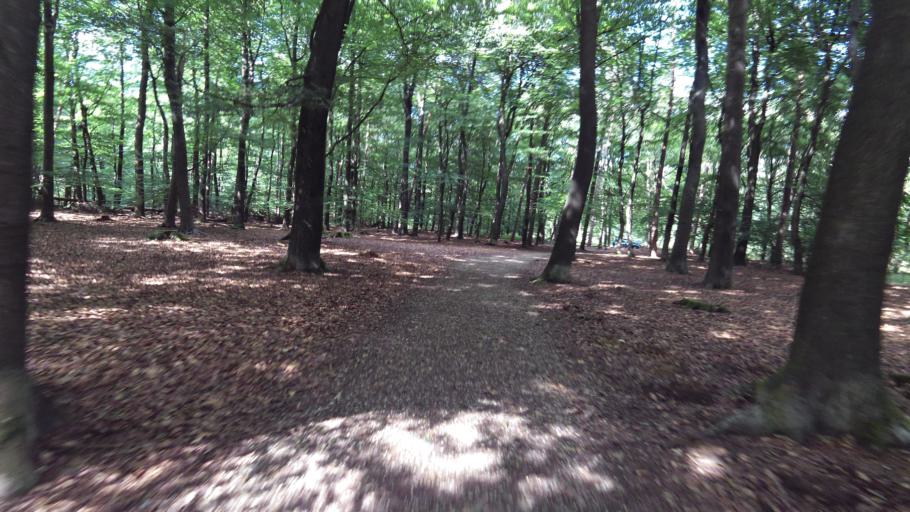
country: NL
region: Gelderland
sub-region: Gemeente Epe
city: Vaassen
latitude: 52.2784
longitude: 5.9214
